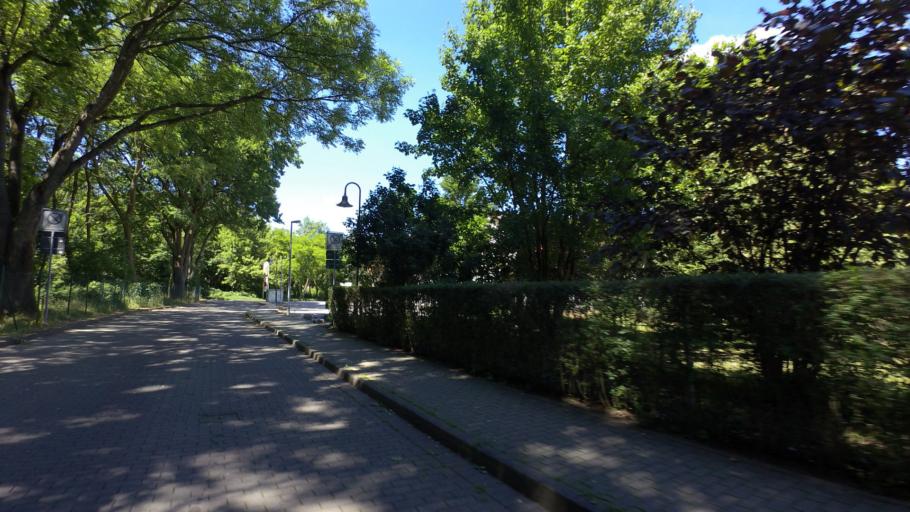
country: DE
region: Brandenburg
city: Zossen
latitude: 52.2179
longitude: 13.4476
